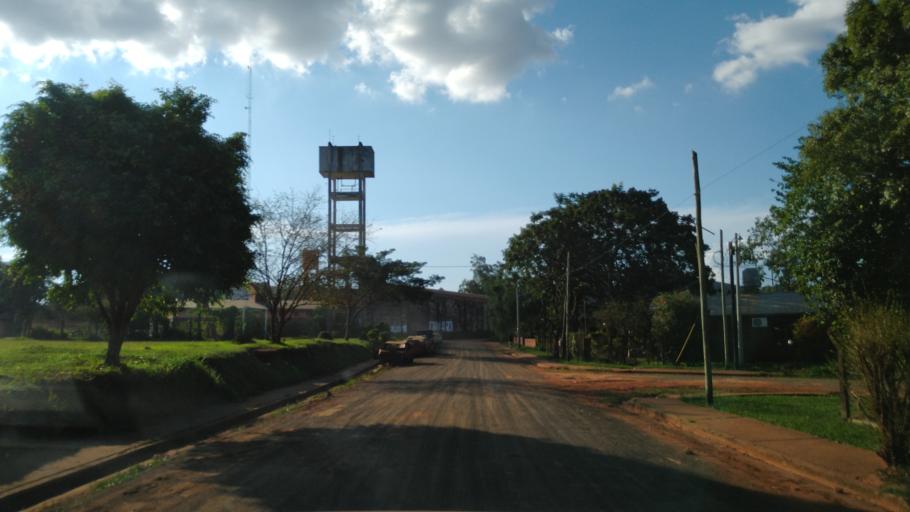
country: AR
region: Misiones
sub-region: Departamento de Capital
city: Posadas
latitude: -27.4047
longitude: -55.9194
